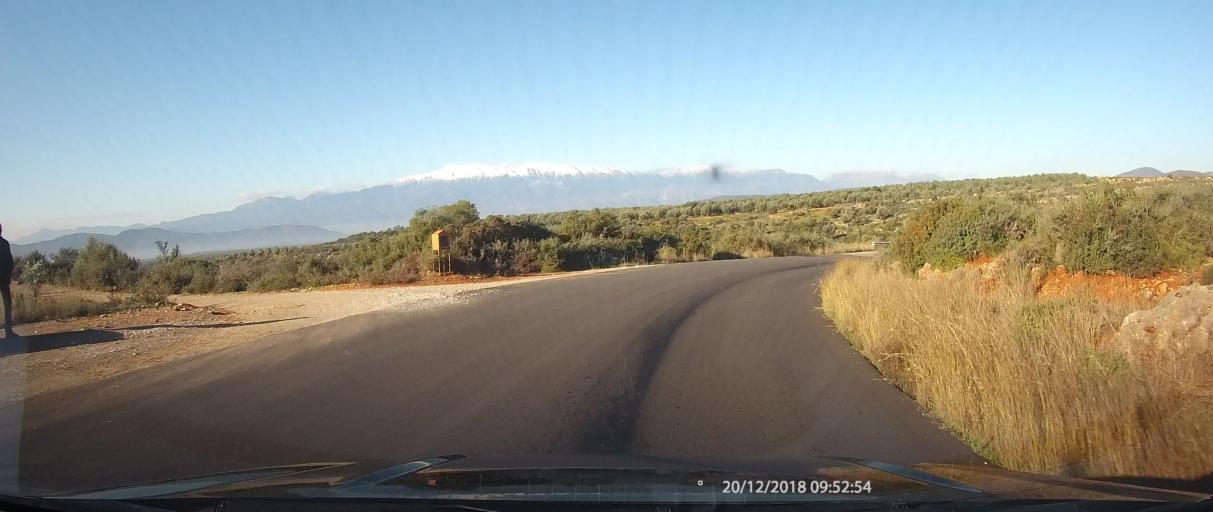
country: GR
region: Peloponnese
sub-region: Nomos Lakonias
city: Yerakion
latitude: 37.0076
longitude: 22.6383
